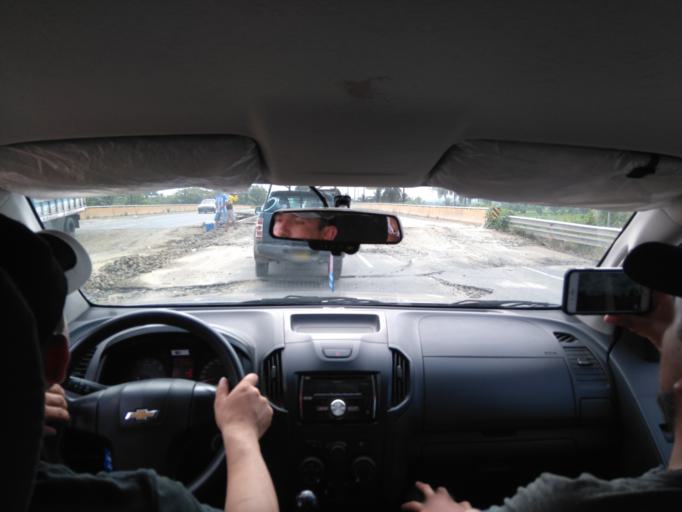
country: EC
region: Manabi
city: Rocafuerte
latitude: -0.9232
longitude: -80.4713
